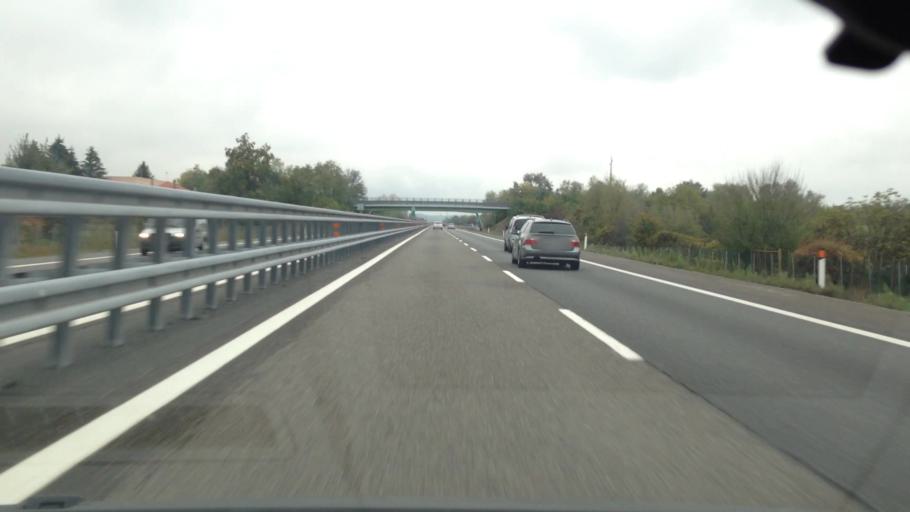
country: IT
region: Piedmont
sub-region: Provincia di Asti
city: Villafranca d'Asti
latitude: 44.9145
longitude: 8.0384
